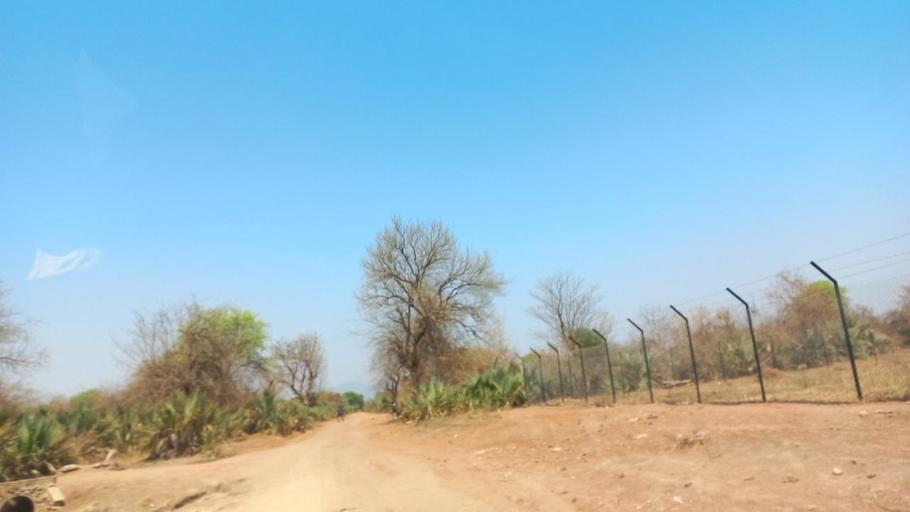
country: ZM
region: Lusaka
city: Luangwa
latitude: -15.1867
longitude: 30.2155
